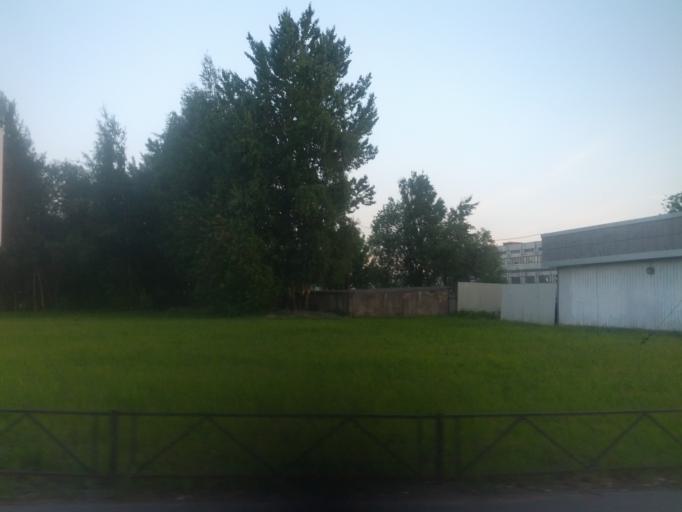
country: RU
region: St.-Petersburg
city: Staraya Derevnya
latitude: 59.9953
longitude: 30.2549
